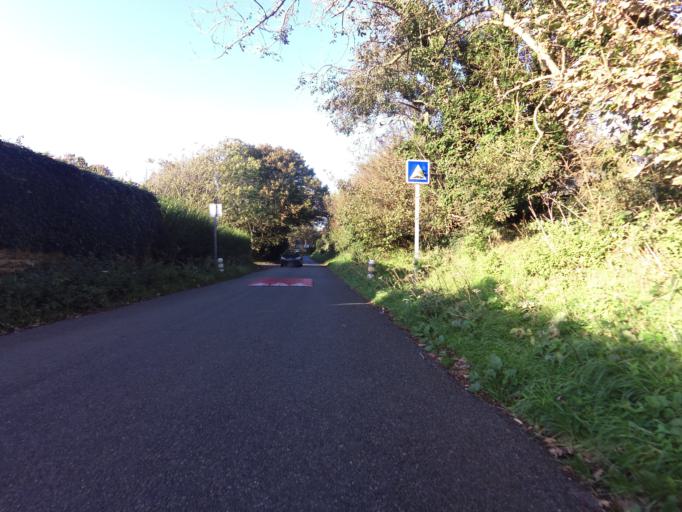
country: FR
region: Nord-Pas-de-Calais
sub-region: Departement du Pas-de-Calais
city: Wimille
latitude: 50.7474
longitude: 1.6204
